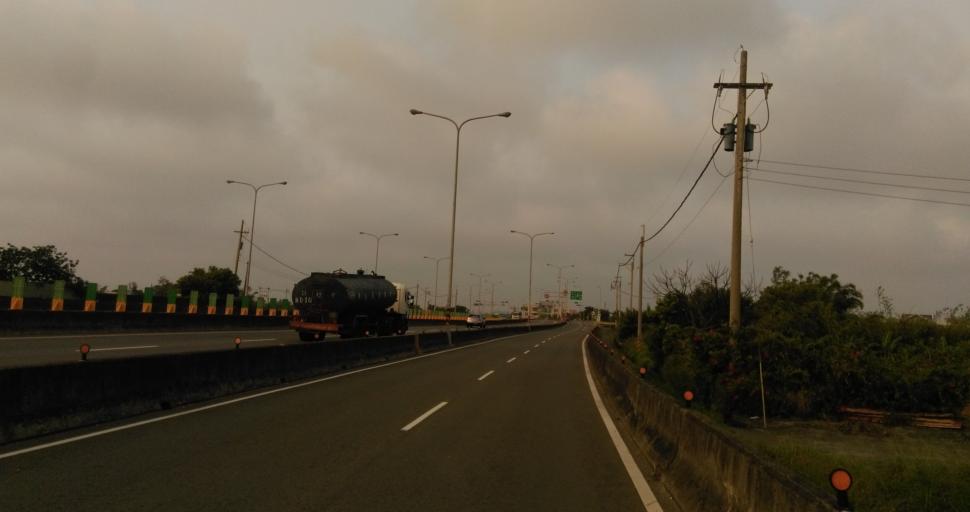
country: TW
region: Taiwan
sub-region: Hsinchu
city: Hsinchu
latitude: 24.7912
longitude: 120.9185
